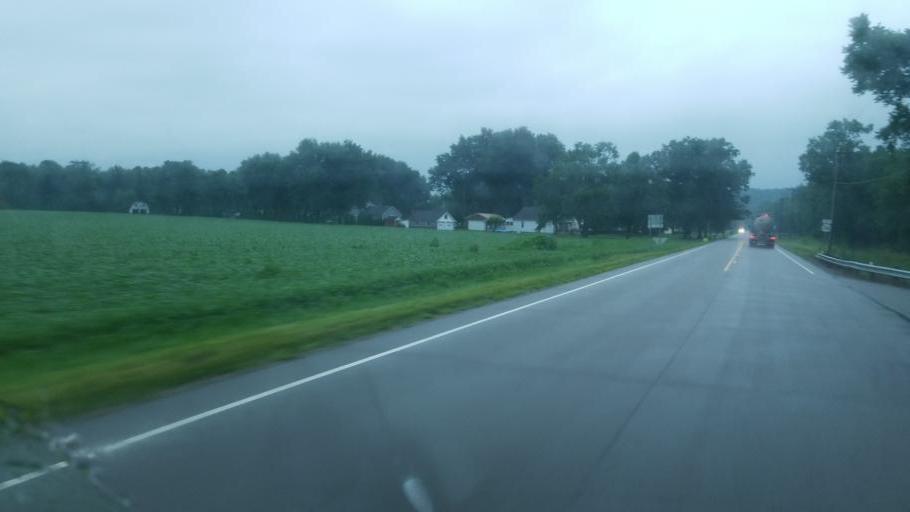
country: US
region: Ohio
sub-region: Coshocton County
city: Coshocton
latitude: 40.3165
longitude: -81.9362
